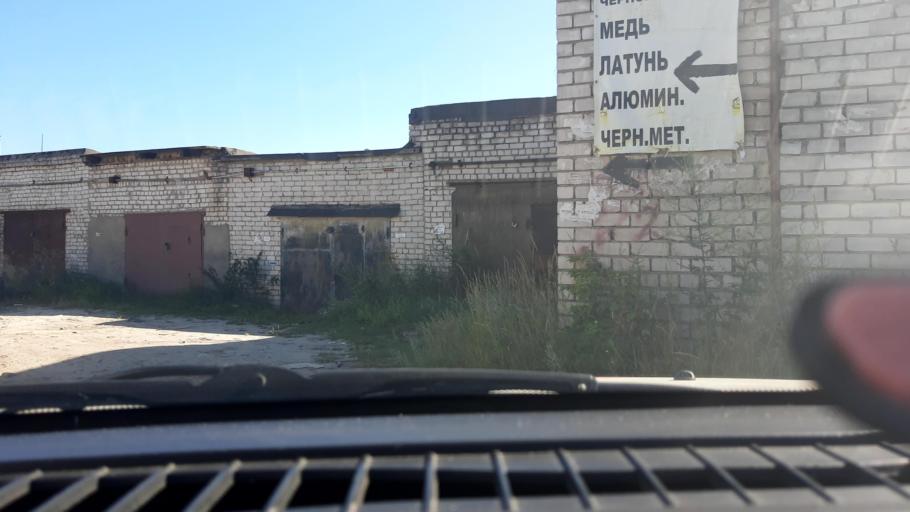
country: RU
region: Nizjnij Novgorod
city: Gorbatovka
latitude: 56.3767
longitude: 43.7989
